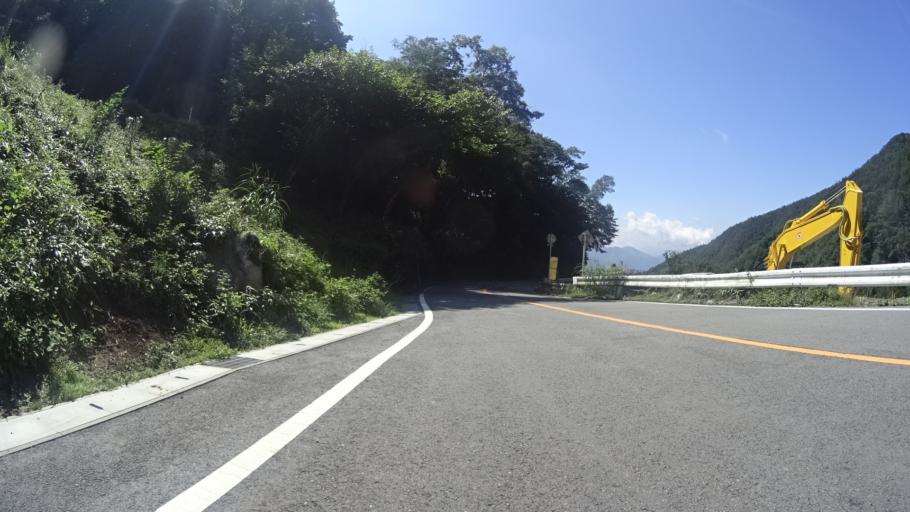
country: JP
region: Yamanashi
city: Enzan
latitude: 35.7726
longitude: 138.8041
